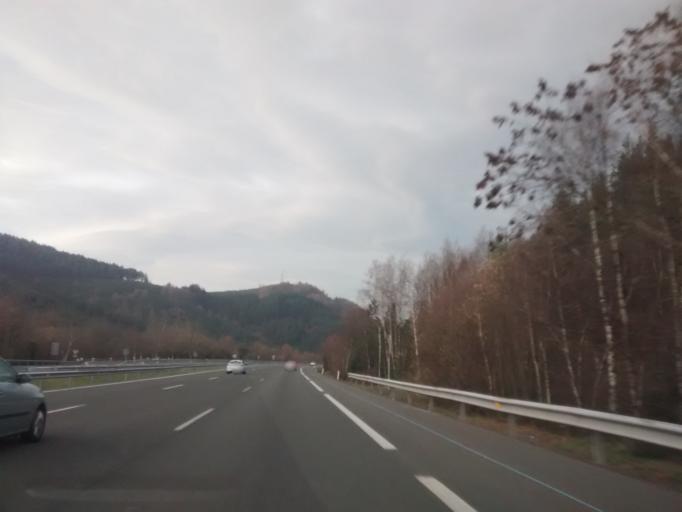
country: ES
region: Basque Country
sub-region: Provincia de Alava
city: Lezama
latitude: 43.0362
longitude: -2.9167
